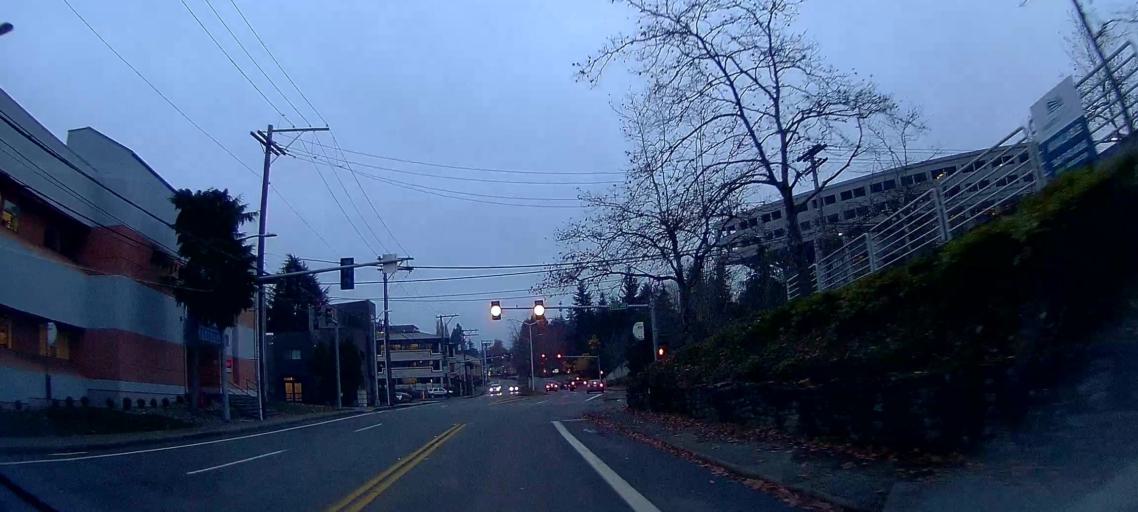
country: US
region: Washington
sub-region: Thurston County
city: Olympia
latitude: 47.0383
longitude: -122.8959
